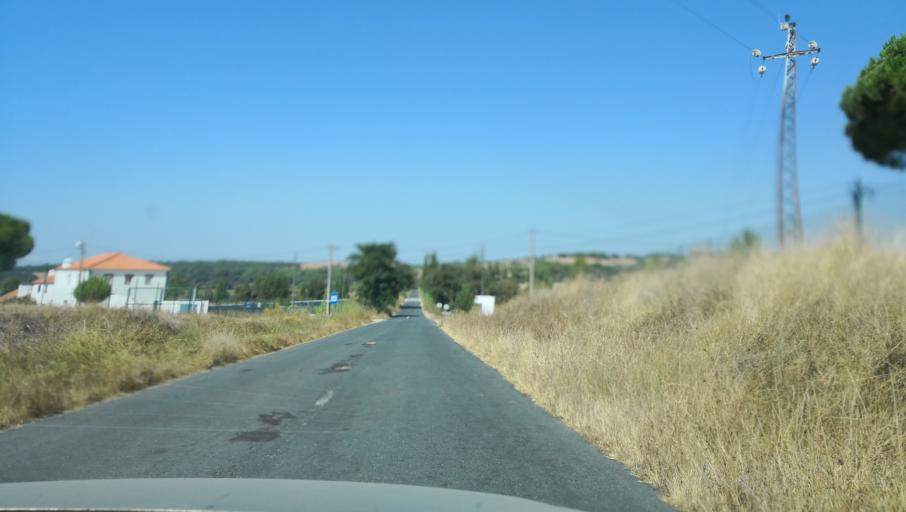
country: PT
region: Setubal
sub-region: Alcacer do Sal
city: Alcacer do Sal
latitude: 38.2831
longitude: -8.3996
